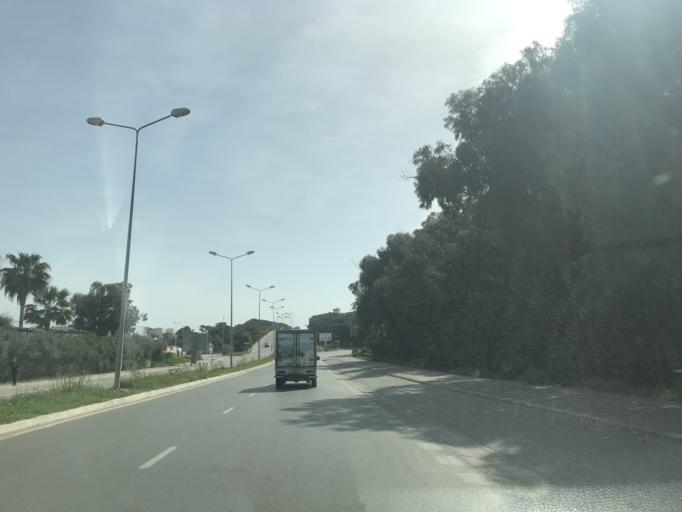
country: TN
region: Tunis
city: Al Marsa
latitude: 36.9202
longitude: 10.2891
